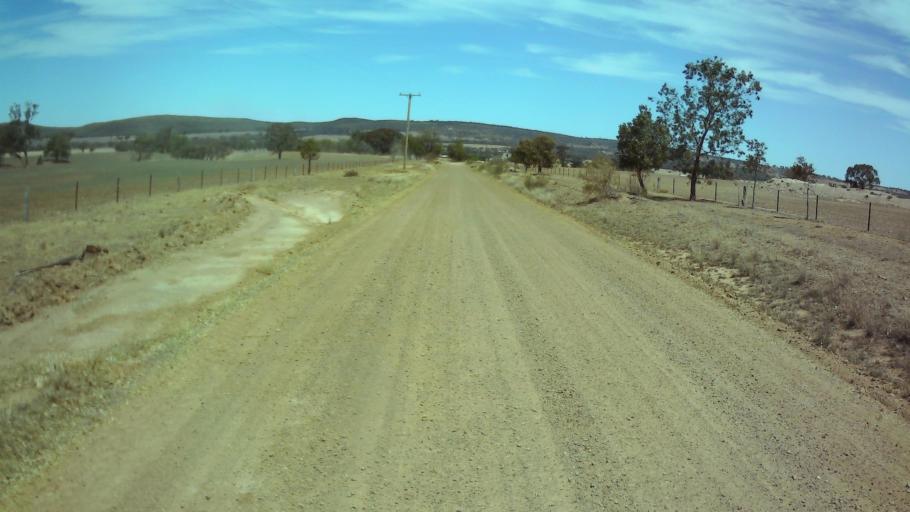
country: AU
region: New South Wales
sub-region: Weddin
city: Grenfell
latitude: -33.8240
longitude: 148.1697
